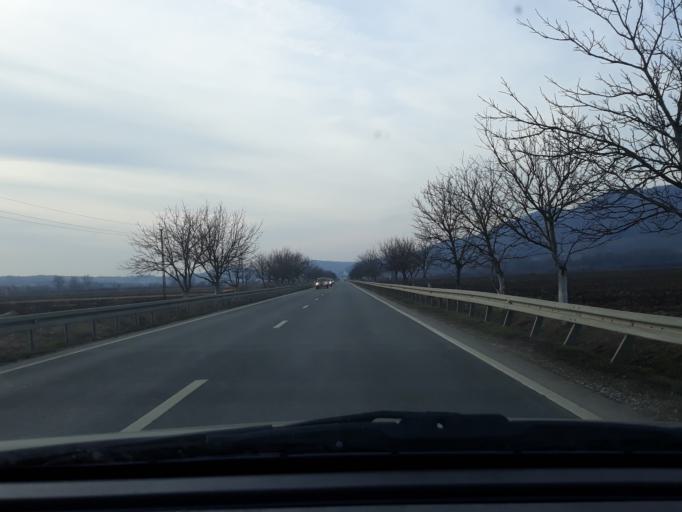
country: RO
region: Salaj
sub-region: Comuna Periceiu
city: Periceiu
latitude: 47.2282
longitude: 22.8473
